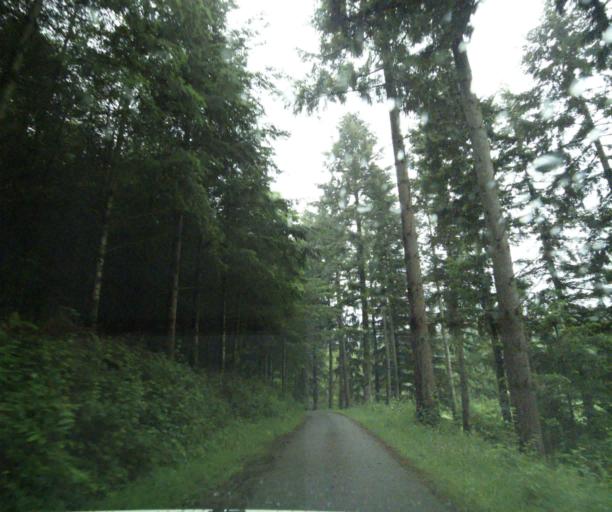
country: FR
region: Bourgogne
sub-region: Departement de Saone-et-Loire
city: La Clayette
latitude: 46.3531
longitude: 4.3637
